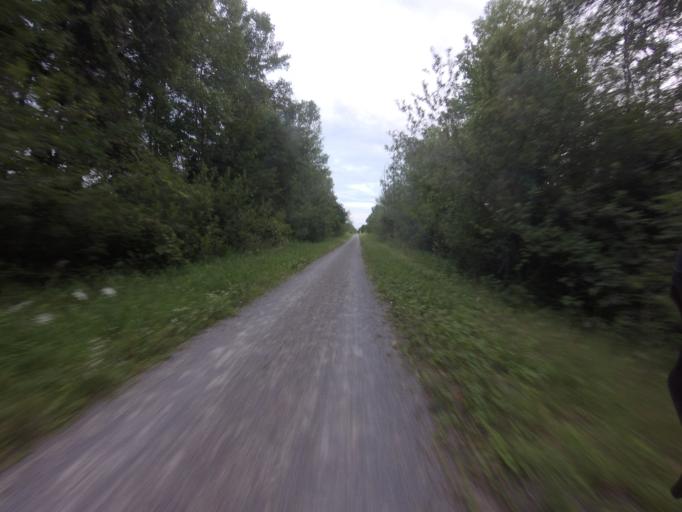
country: CA
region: Ontario
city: Carleton Place
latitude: 45.1525
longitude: -76.0983
